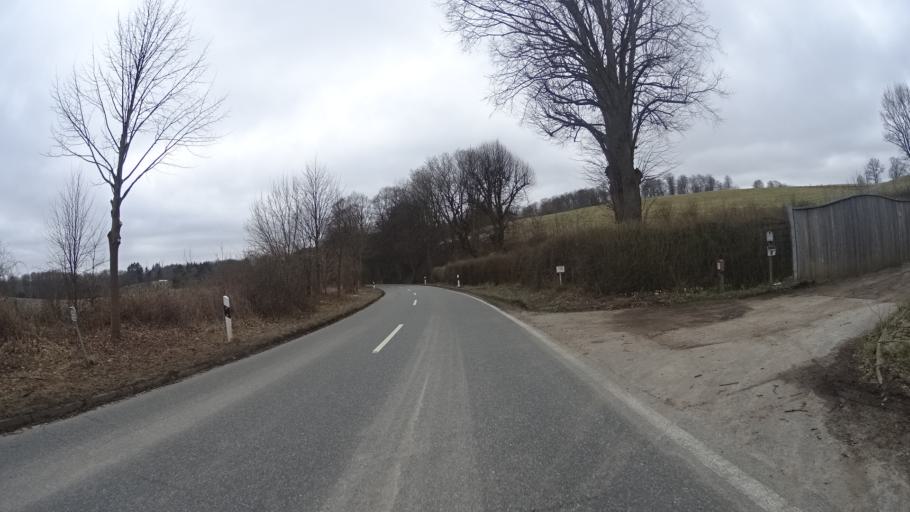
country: DE
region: Schleswig-Holstein
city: Malente
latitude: 54.1737
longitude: 10.5250
